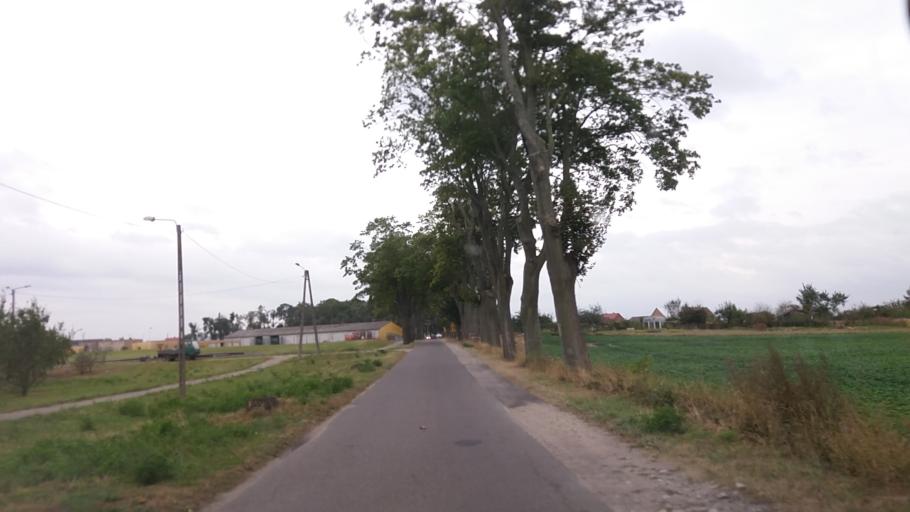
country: PL
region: West Pomeranian Voivodeship
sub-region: Powiat choszczenski
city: Bierzwnik
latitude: 52.9739
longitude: 15.5792
